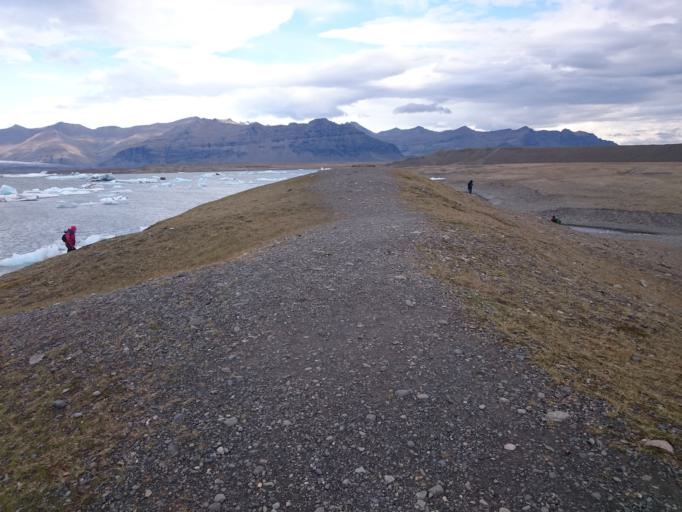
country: IS
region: East
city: Hoefn
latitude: 64.0524
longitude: -16.1786
